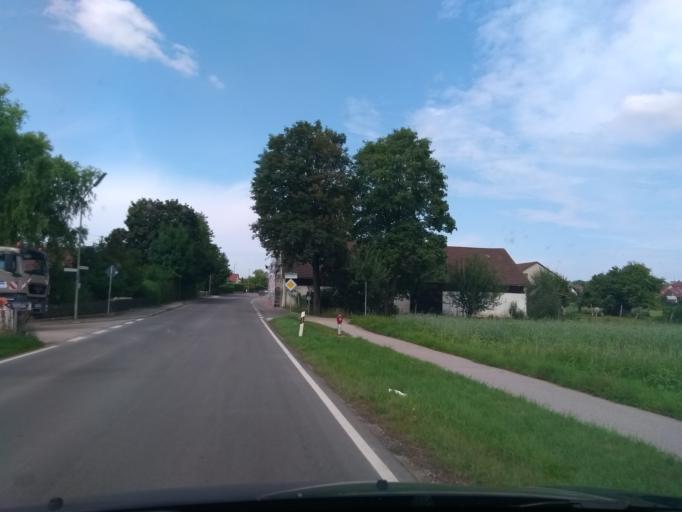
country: DE
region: Bavaria
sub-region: Upper Bavaria
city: Markt Indersdorf
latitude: 48.3490
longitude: 11.3836
